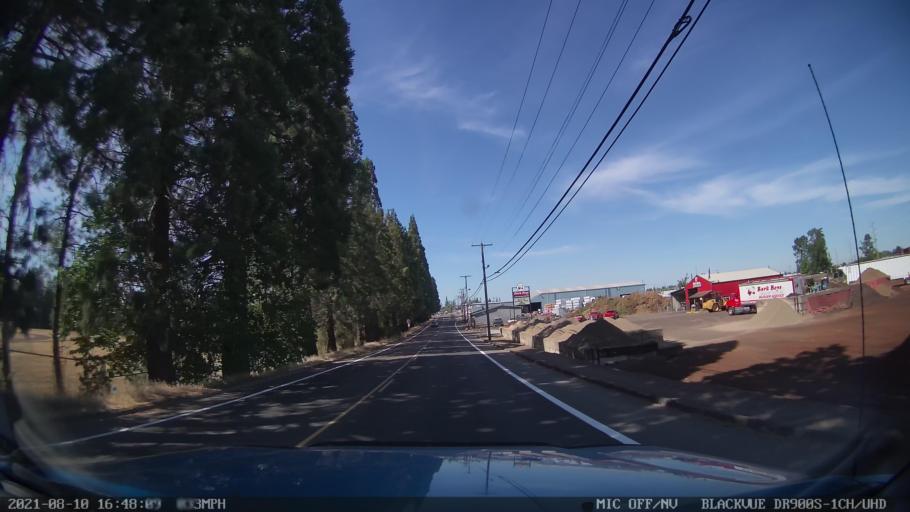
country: US
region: Oregon
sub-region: Marion County
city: Keizer
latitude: 44.9668
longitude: -123.0194
